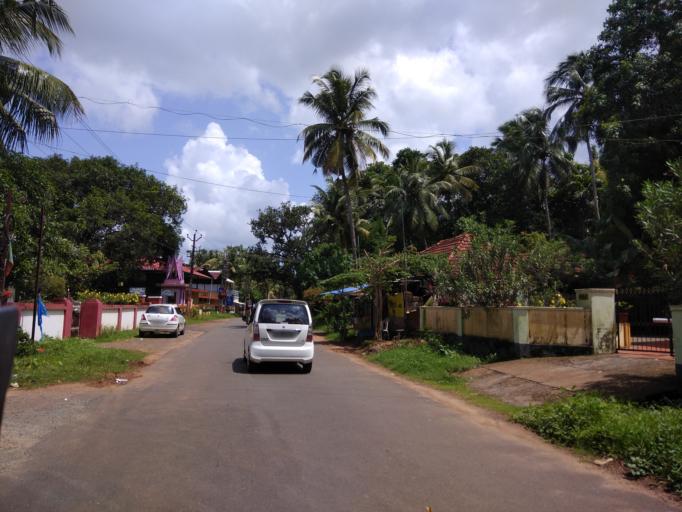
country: IN
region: Kerala
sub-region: Thrissur District
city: Avanoor
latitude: 10.5470
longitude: 76.1483
